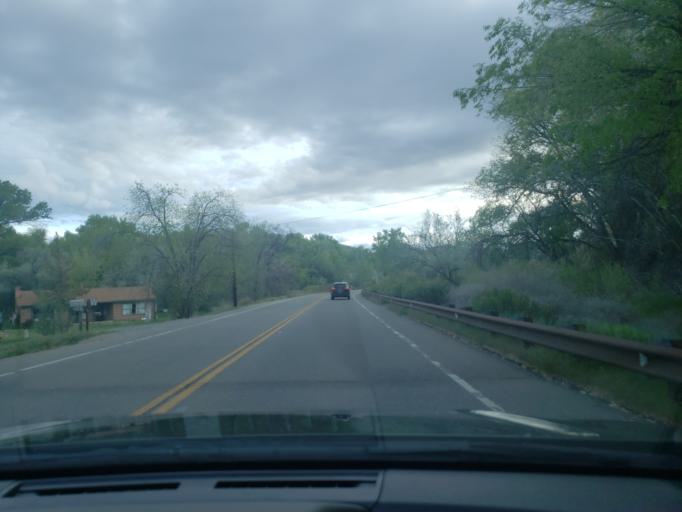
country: US
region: Colorado
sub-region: Mesa County
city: Grand Junction
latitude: 39.0601
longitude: -108.5891
